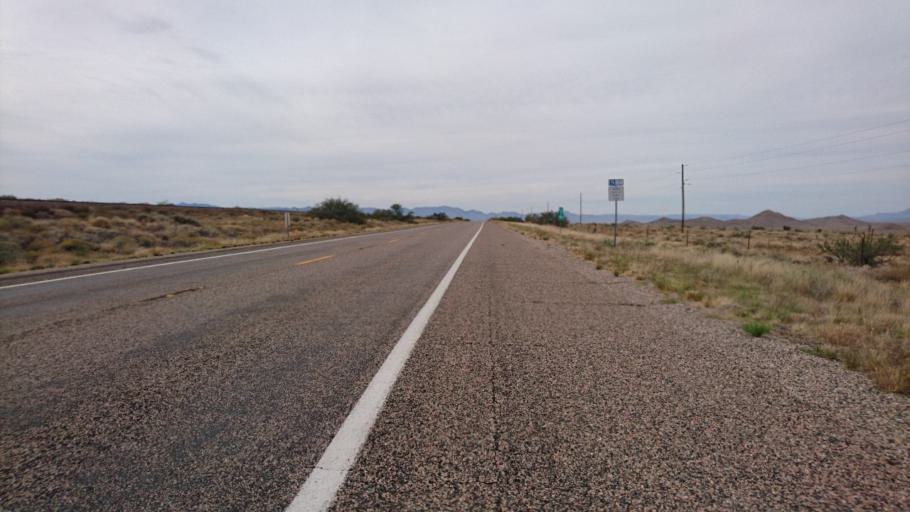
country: US
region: Arizona
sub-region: Mohave County
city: New Kingman-Butler
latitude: 35.4142
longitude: -113.7874
